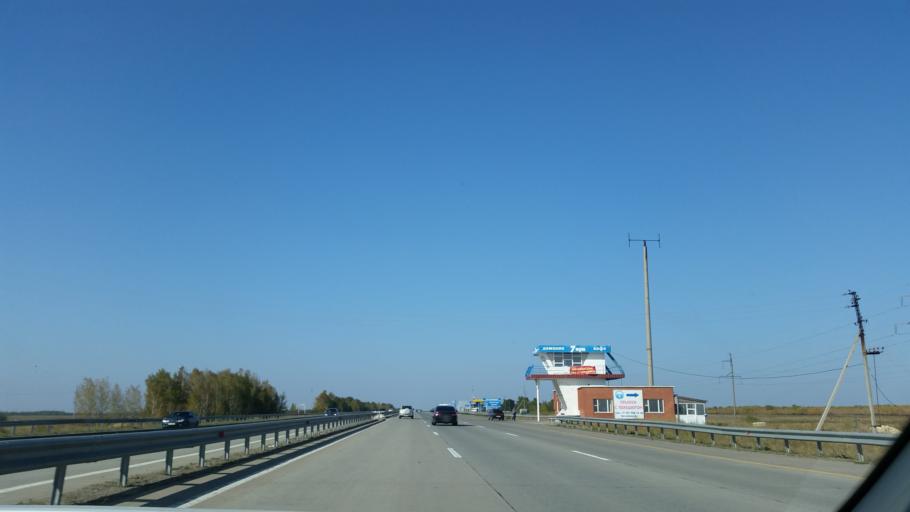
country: KZ
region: Astana Qalasy
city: Astana
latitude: 51.3039
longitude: 71.3544
